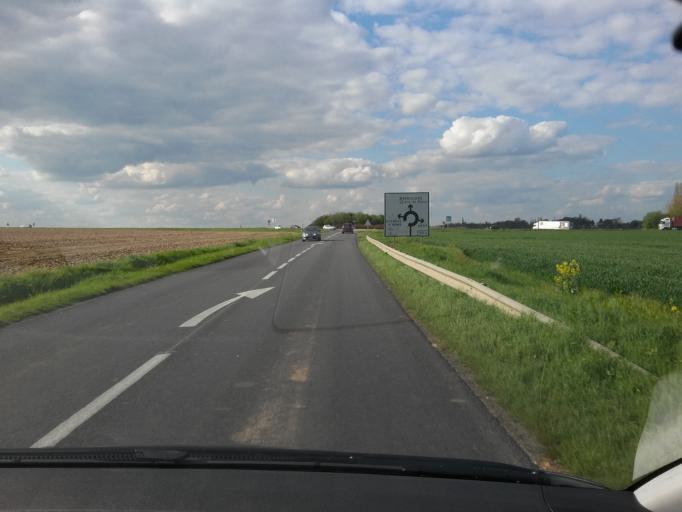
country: FR
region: Picardie
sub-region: Departement de l'Oise
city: Estrees-Saint-Denis
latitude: 49.4016
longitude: 2.6508
